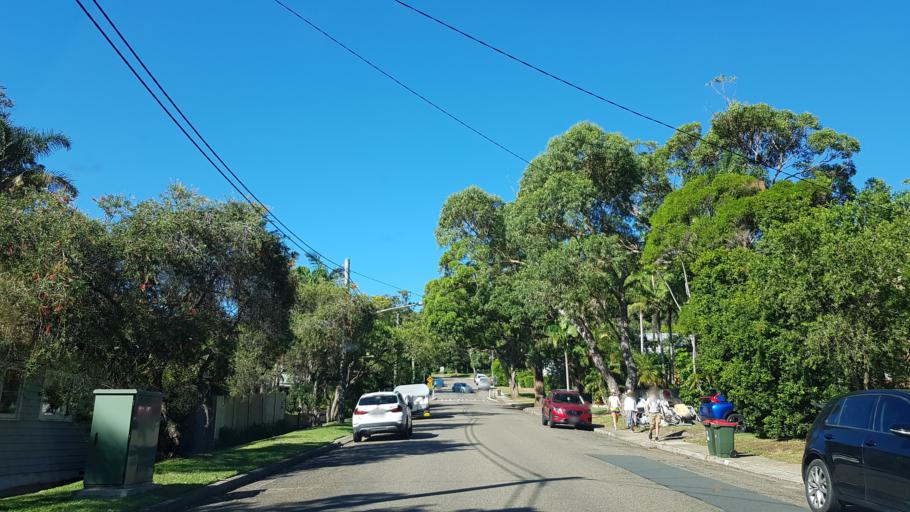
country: AU
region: New South Wales
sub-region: Pittwater
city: Bilgola Beach
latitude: -33.6234
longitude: 151.3362
